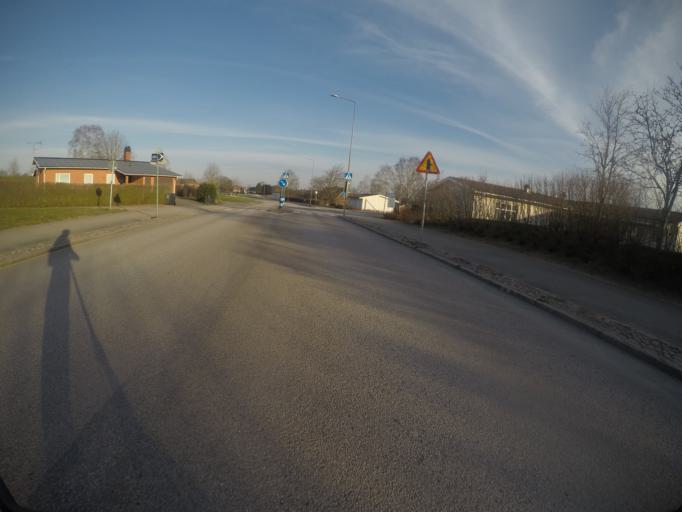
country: SE
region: Halland
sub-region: Laholms Kommun
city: Laholm
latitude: 56.5053
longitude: 13.0315
